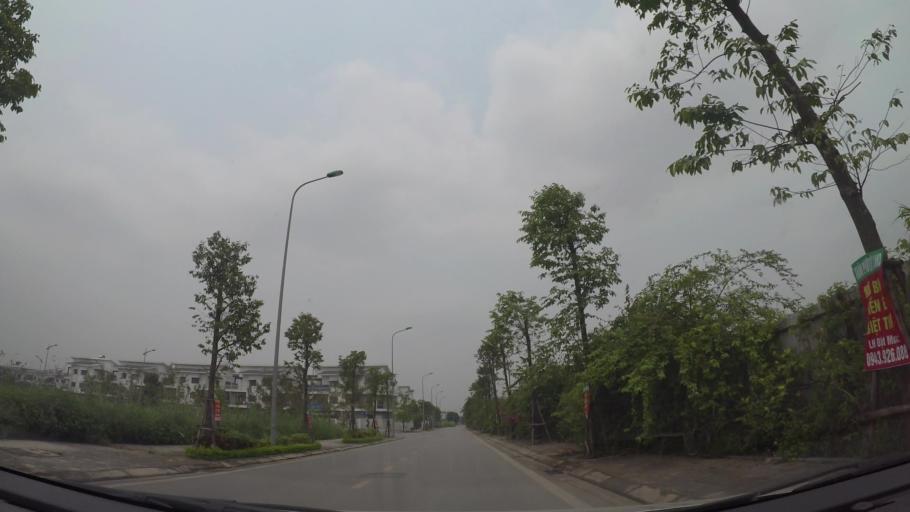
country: VN
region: Ha Noi
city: Cau Dien
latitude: 21.0278
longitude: 105.7480
